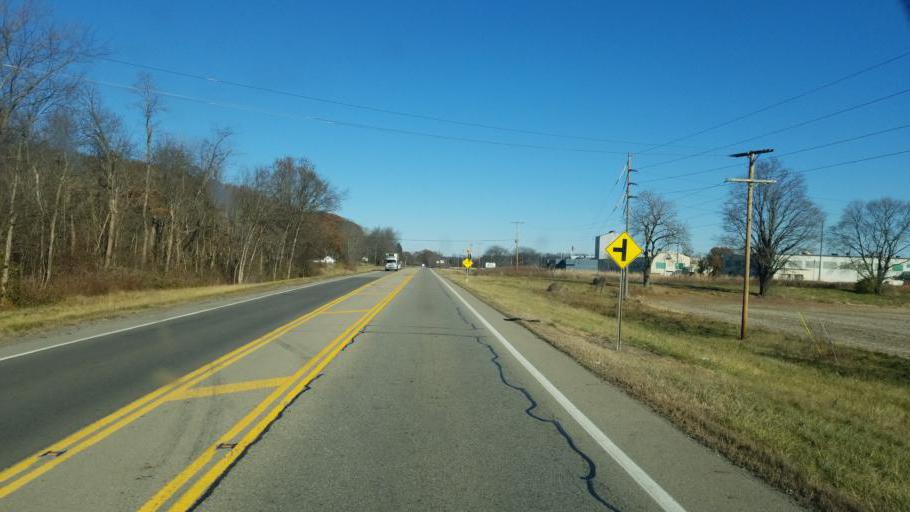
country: US
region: Ohio
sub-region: Coshocton County
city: Coshocton
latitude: 40.2042
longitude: -81.8873
